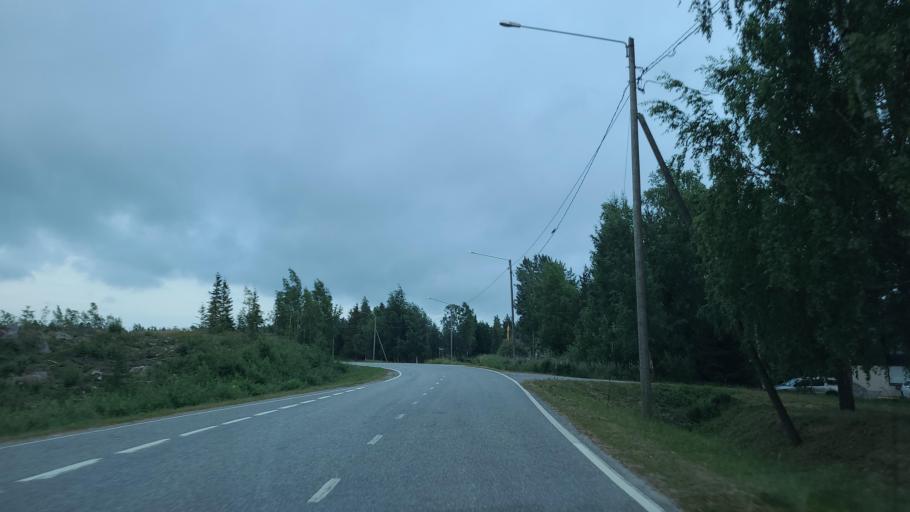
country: FI
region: Ostrobothnia
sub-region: Vaasa
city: Replot
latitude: 63.2829
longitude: 21.1261
